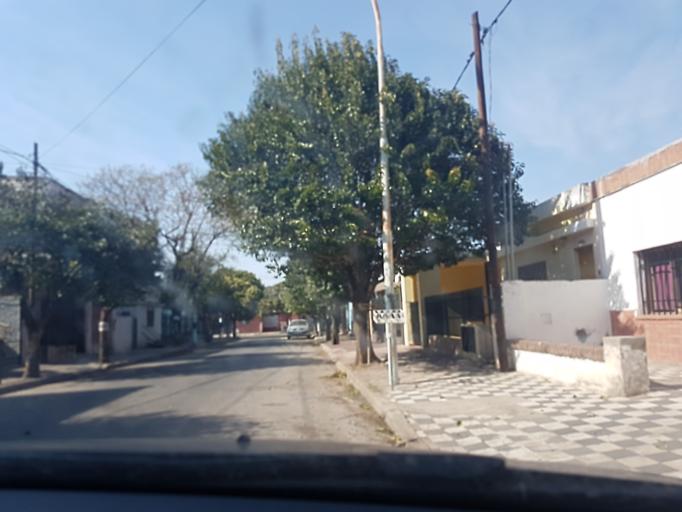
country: AR
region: Cordoba
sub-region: Departamento de Capital
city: Cordoba
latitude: -31.4389
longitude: -64.1531
